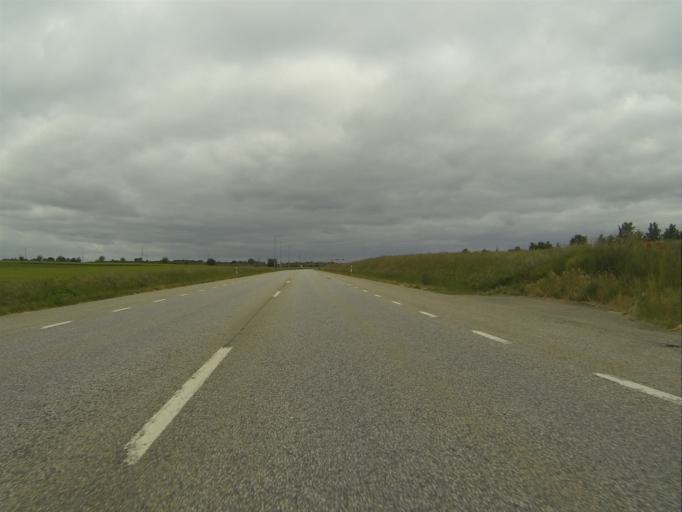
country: SE
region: Skane
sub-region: Staffanstorps Kommun
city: Hjaerup
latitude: 55.6404
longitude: 13.1152
